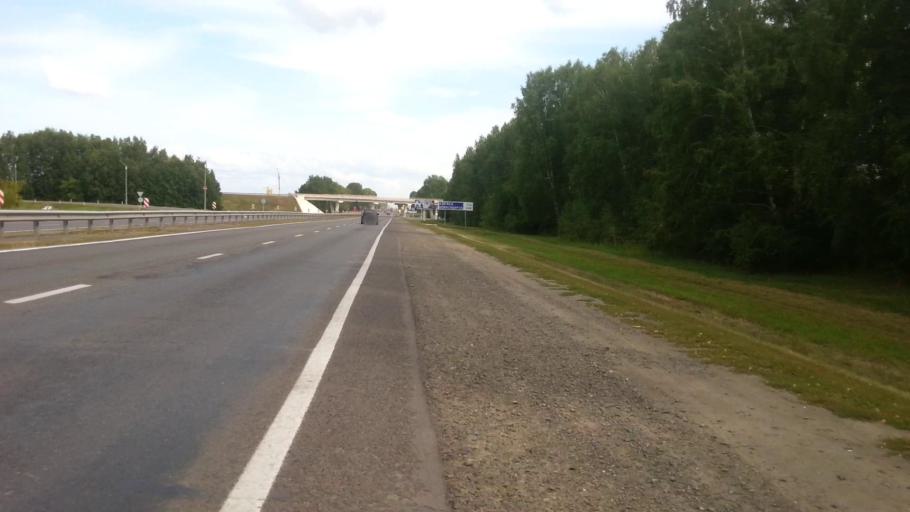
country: RU
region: Altai Krai
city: Vlasikha
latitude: 53.3539
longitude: 83.5485
